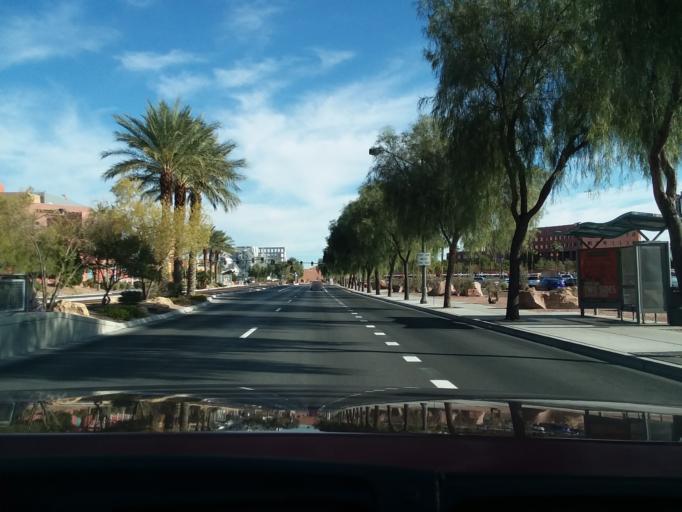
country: US
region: Nevada
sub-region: Clark County
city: Las Vegas
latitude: 36.1636
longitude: -115.1564
